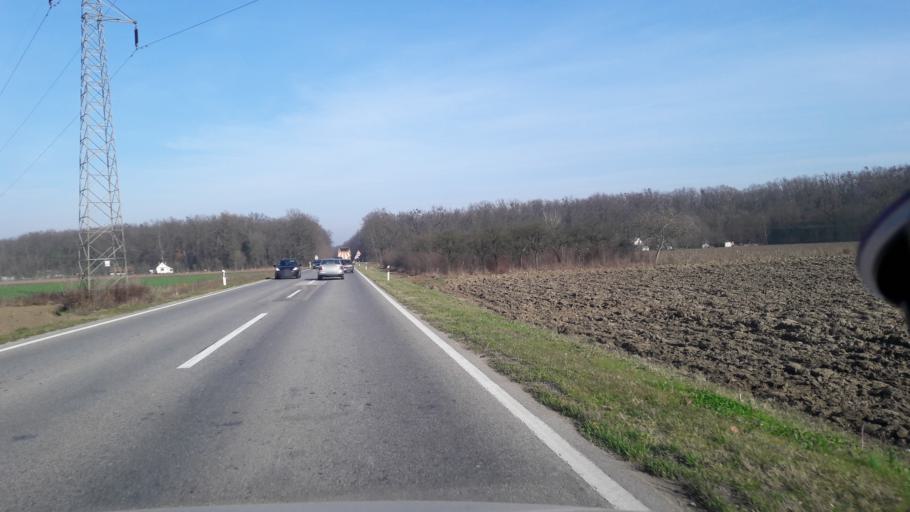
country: HR
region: Vukovarsko-Srijemska
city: Gradiste
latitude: 45.1174
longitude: 18.7075
